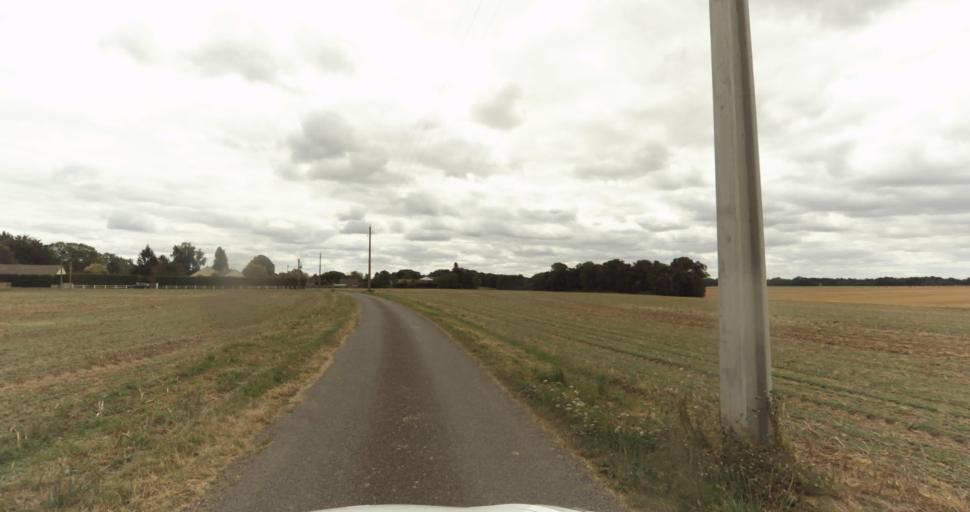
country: FR
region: Haute-Normandie
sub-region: Departement de l'Eure
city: La Madeleine-de-Nonancourt
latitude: 48.8386
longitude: 1.2391
